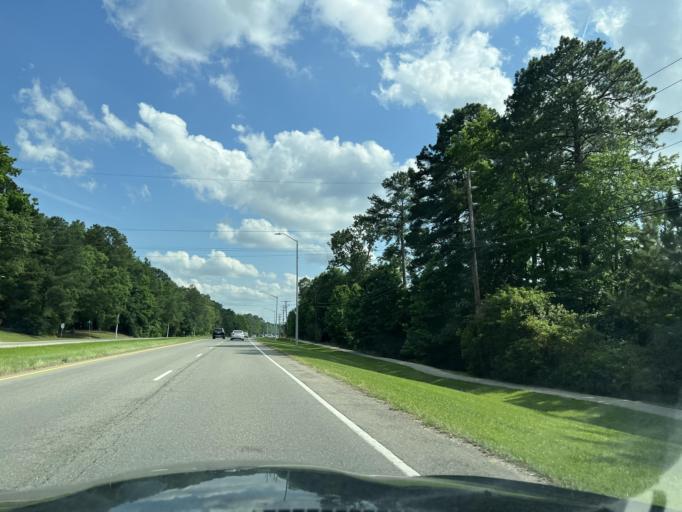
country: US
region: North Carolina
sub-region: Durham County
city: Durham
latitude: 35.9409
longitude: -78.8875
